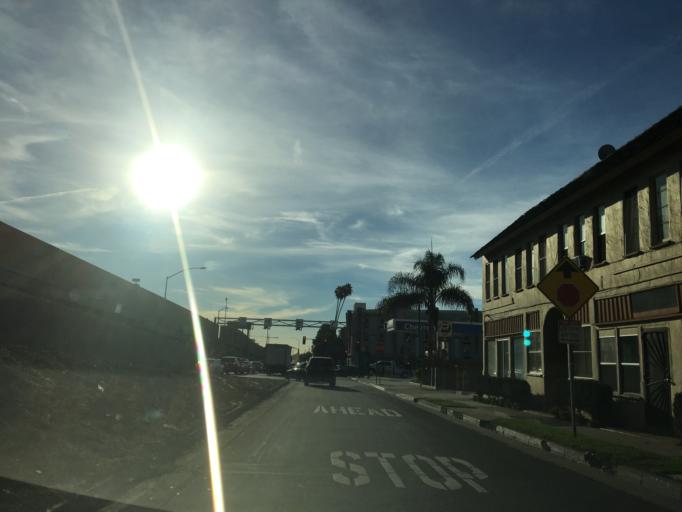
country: US
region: California
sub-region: Los Angeles County
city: Westwood, Los Angeles
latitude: 34.0477
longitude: -118.4480
